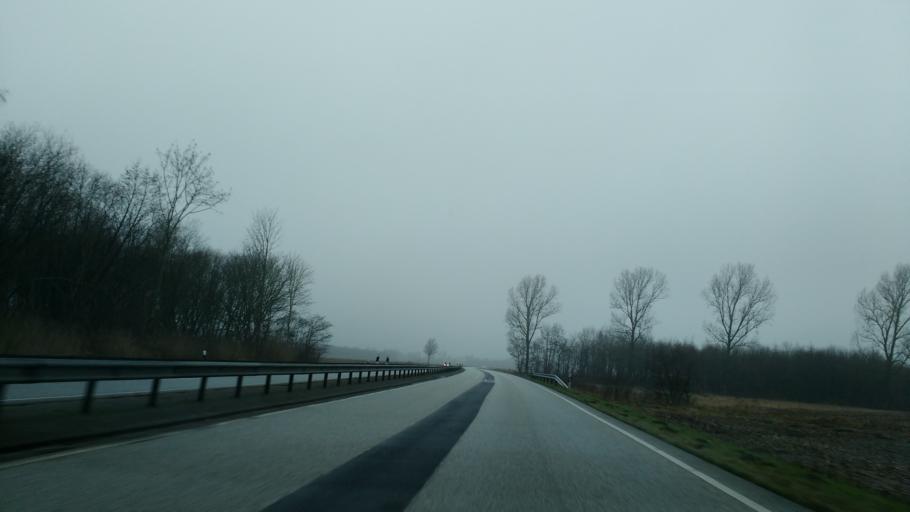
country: DE
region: Schleswig-Holstein
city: Jevenstedt
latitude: 54.2405
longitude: 9.6756
